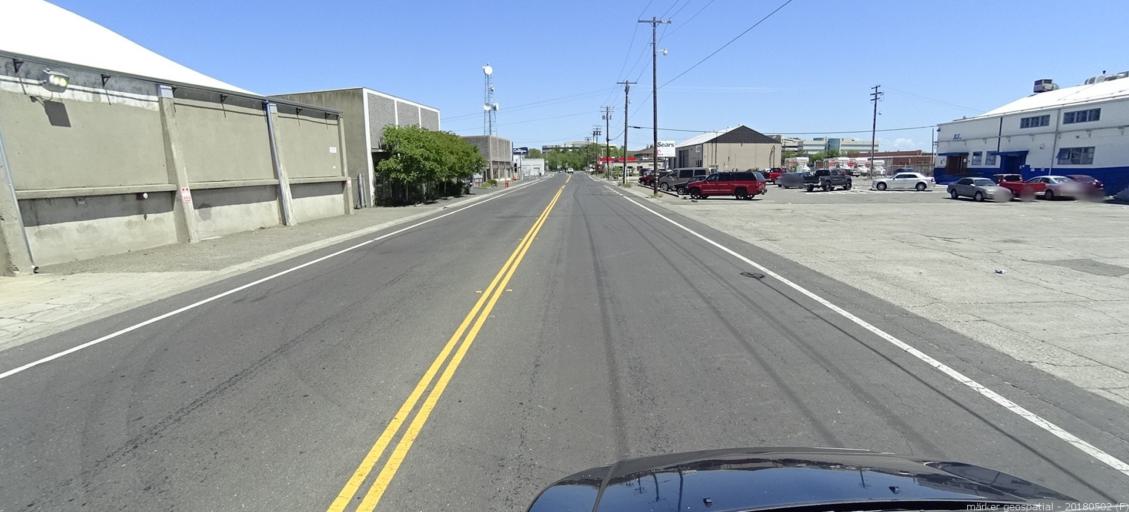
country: US
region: California
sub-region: Sacramento County
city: Sacramento
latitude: 38.6033
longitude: -121.4397
